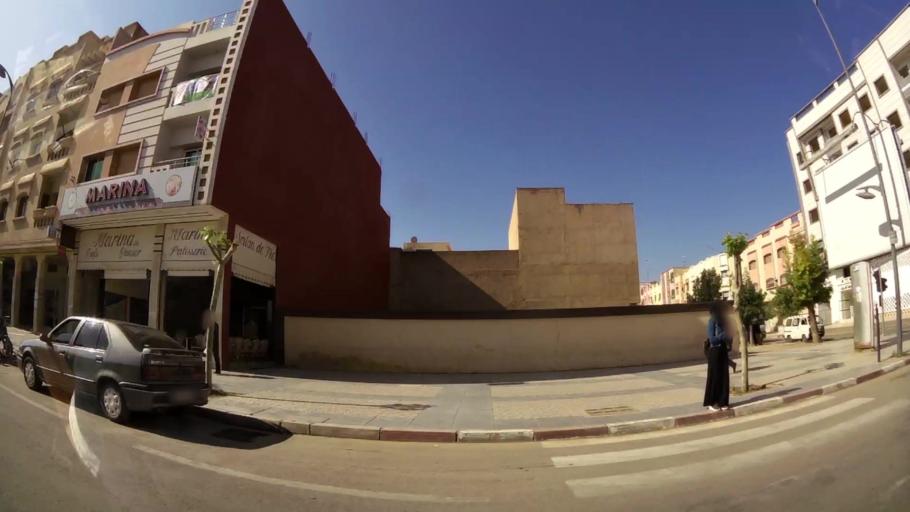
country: MA
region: Oriental
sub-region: Oujda-Angad
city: Oujda
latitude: 34.6814
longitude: -1.9383
